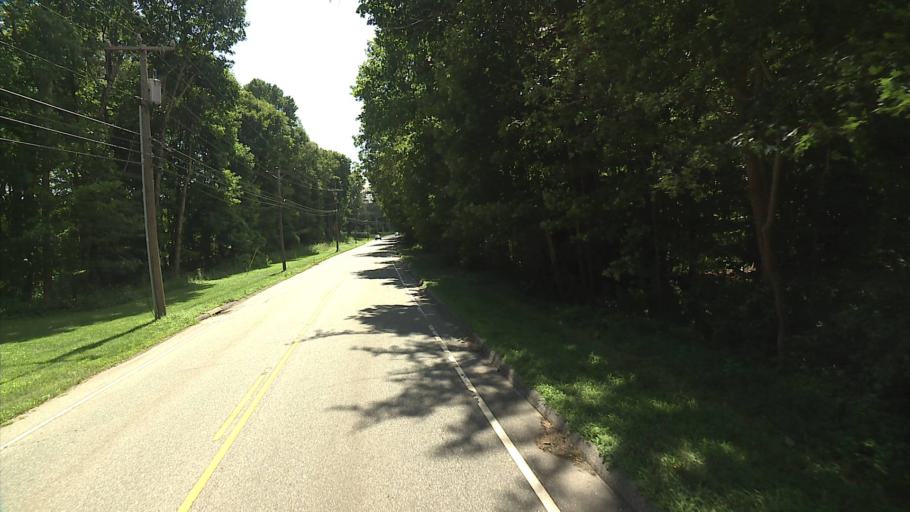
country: US
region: Connecticut
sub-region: Windham County
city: Windham
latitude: 41.6945
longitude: -72.1564
